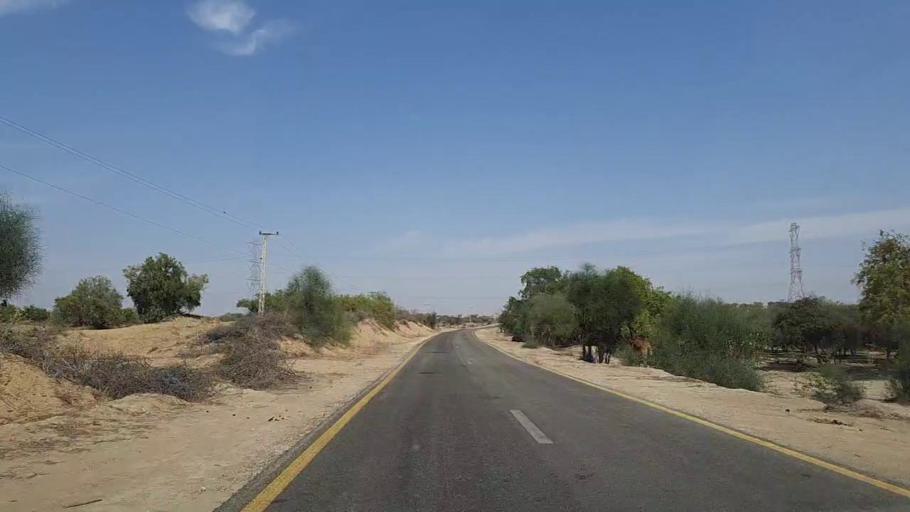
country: PK
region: Sindh
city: Mithi
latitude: 24.8489
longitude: 69.8373
